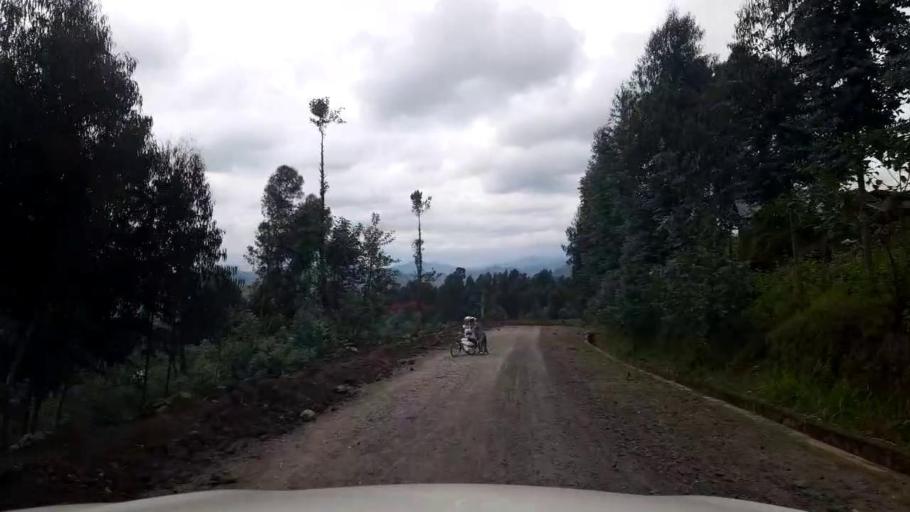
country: RW
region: Northern Province
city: Musanze
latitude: -1.5364
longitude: 29.5333
